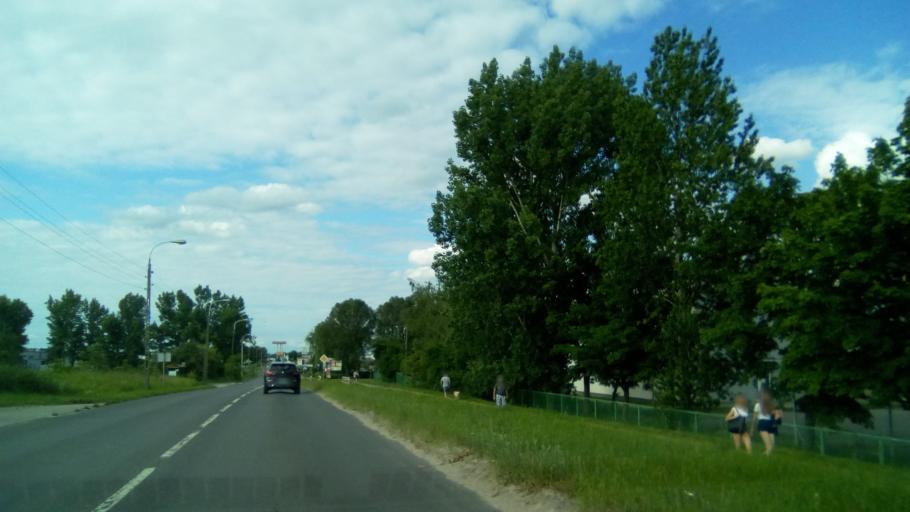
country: PL
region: Greater Poland Voivodeship
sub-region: Powiat gnieznienski
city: Gniezno
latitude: 52.5557
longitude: 17.6066
